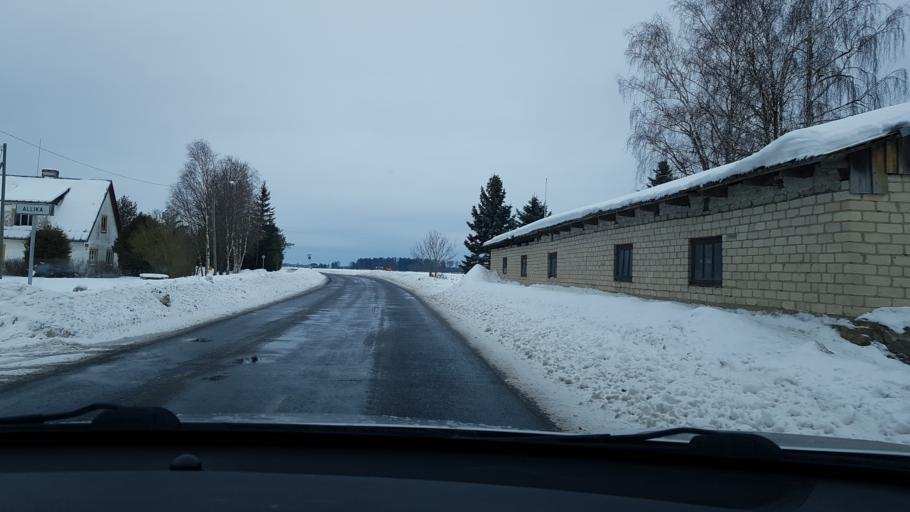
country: EE
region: Jaervamaa
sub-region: Jaerva-Jaani vald
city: Jarva-Jaani
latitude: 59.1497
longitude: 25.7524
